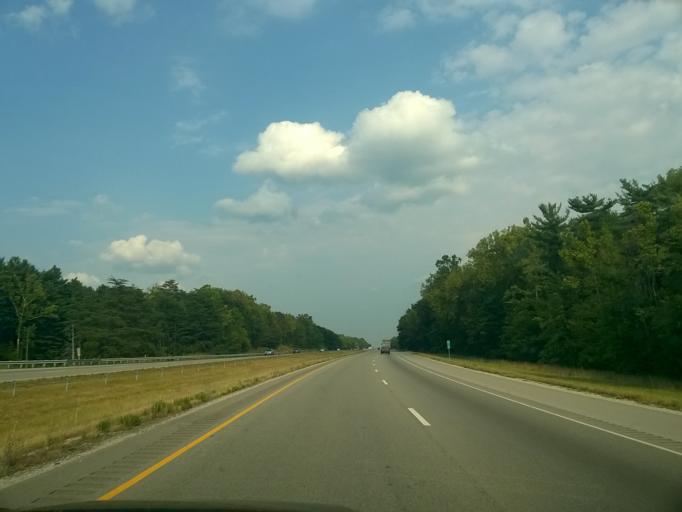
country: US
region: Indiana
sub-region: Vigo County
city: Seelyville
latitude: 39.4511
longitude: -87.1933
